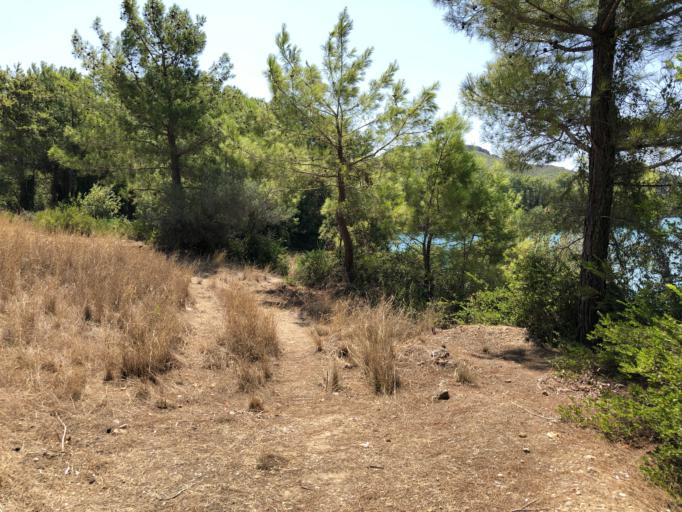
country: TR
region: Antalya
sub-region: Manavgat
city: Manavgat
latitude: 36.8430
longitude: 31.5285
